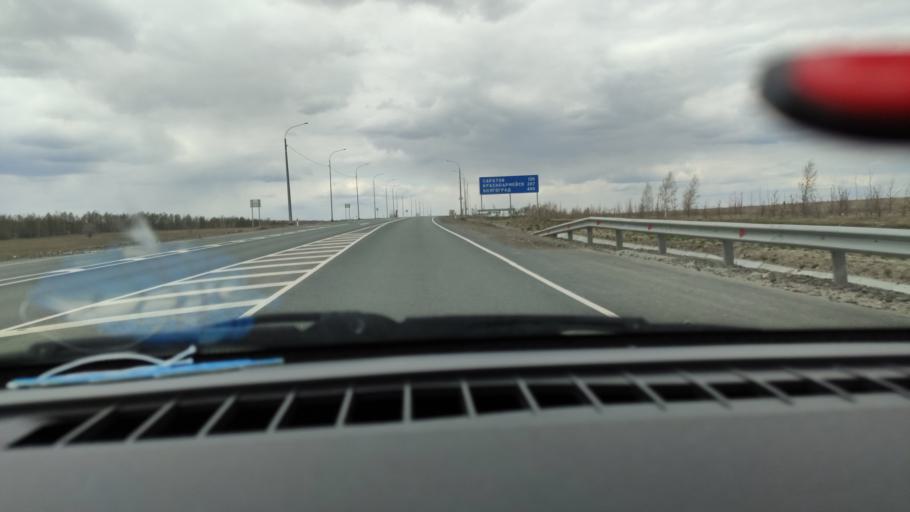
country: RU
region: Saratov
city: Shikhany
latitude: 52.1324
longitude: 47.2268
